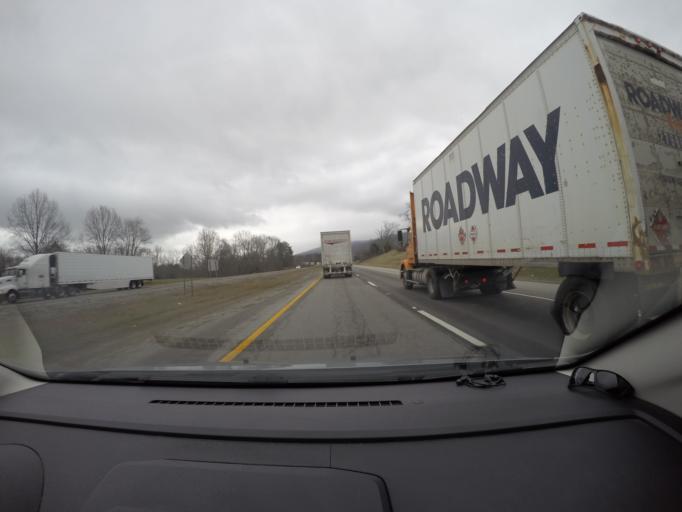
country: US
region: Tennessee
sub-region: Marion County
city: Monteagle
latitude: 35.2846
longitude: -85.8938
